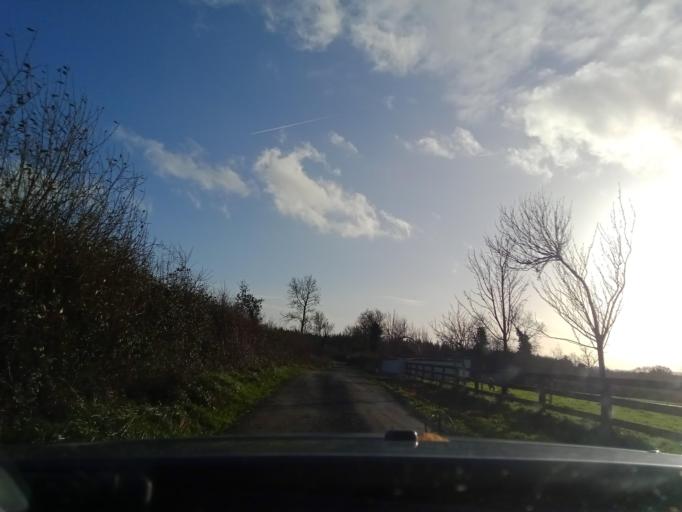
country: IE
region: Leinster
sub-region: Kilkenny
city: Callan
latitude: 52.5202
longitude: -7.4006
